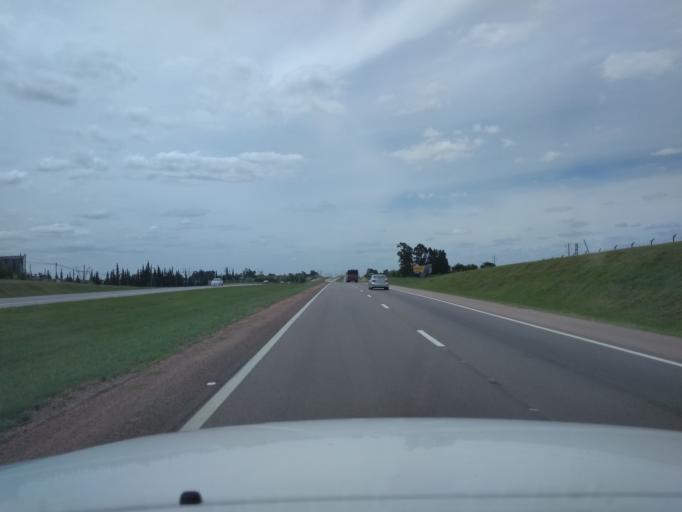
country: UY
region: Canelones
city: Las Piedras
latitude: -34.7333
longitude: -56.2493
